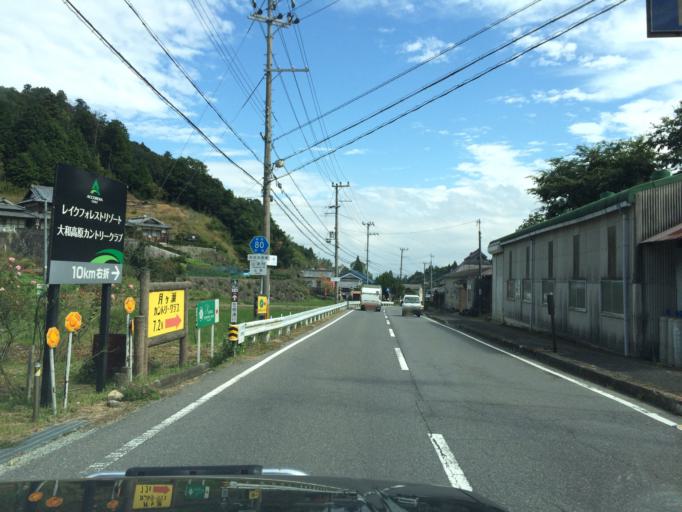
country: JP
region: Mie
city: Nabari
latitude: 34.6787
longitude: 135.9895
